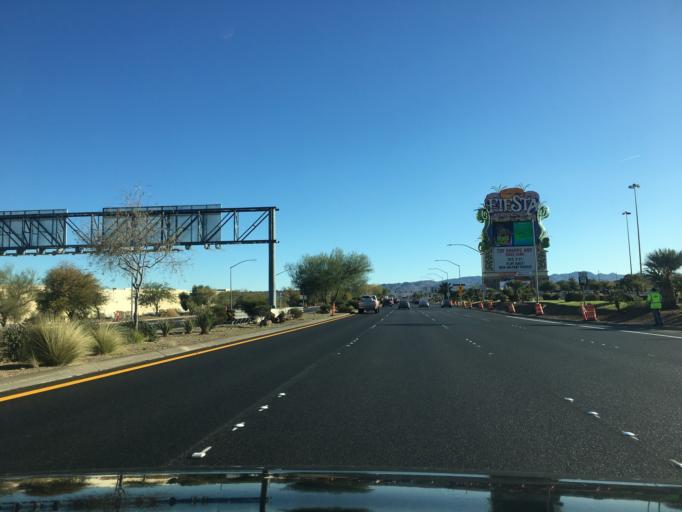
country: US
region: Nevada
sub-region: Clark County
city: Henderson
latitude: 36.0336
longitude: -115.0123
